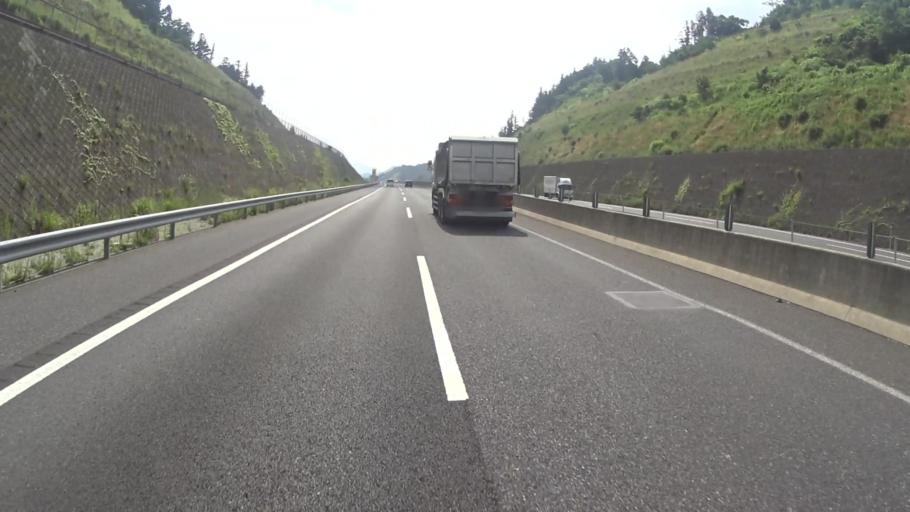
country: JP
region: Shiga Prefecture
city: Hino
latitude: 34.9195
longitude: 136.2759
